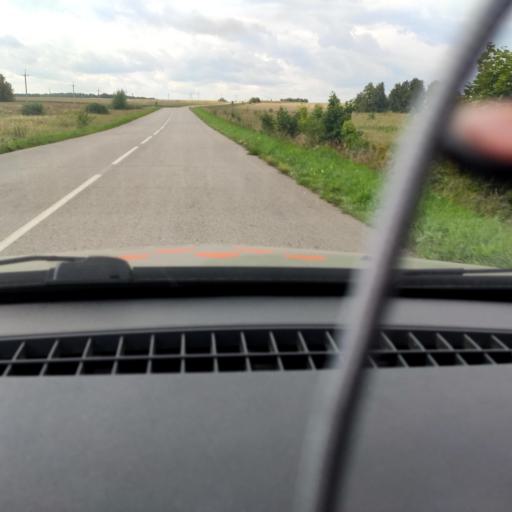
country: RU
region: Bashkortostan
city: Iglino
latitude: 54.7624
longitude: 56.5602
